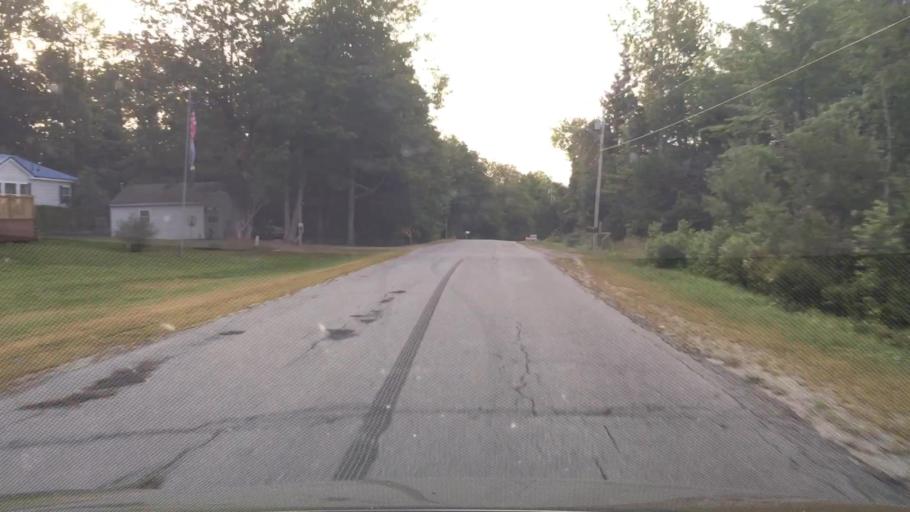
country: US
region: Maine
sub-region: Waldo County
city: Stockton Springs
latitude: 44.4929
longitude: -68.8706
